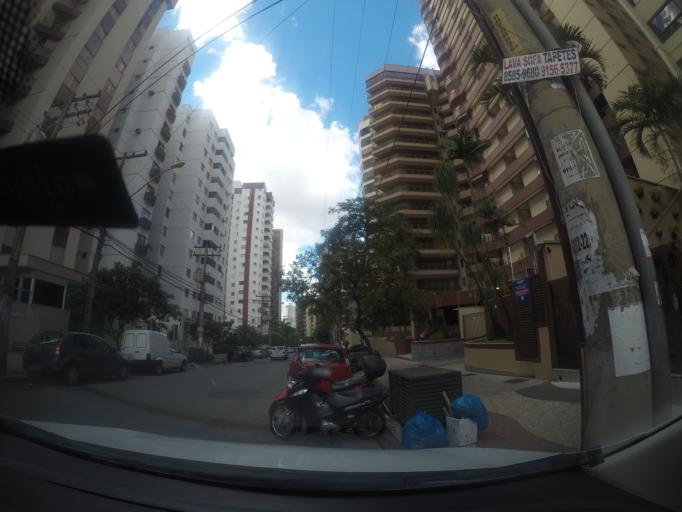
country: BR
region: Goias
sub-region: Goiania
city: Goiania
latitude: -16.7255
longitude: -49.2693
